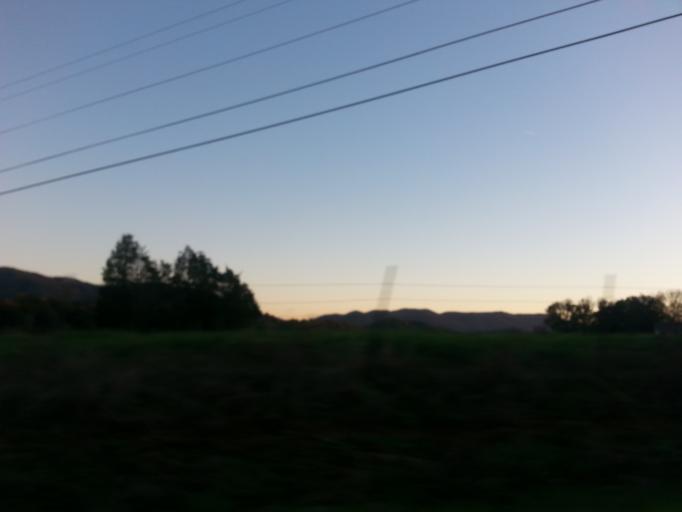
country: US
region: Tennessee
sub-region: Blount County
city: Wildwood
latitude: 35.7803
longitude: -83.8238
